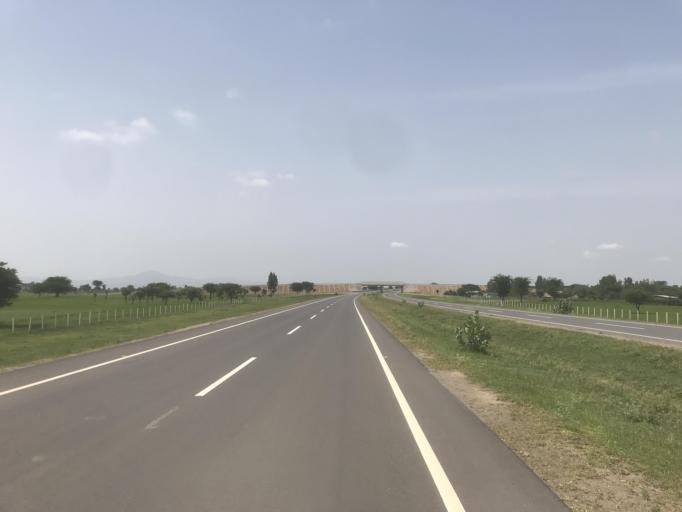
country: ET
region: Oromiya
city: Mojo
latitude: 8.4810
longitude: 39.0506
